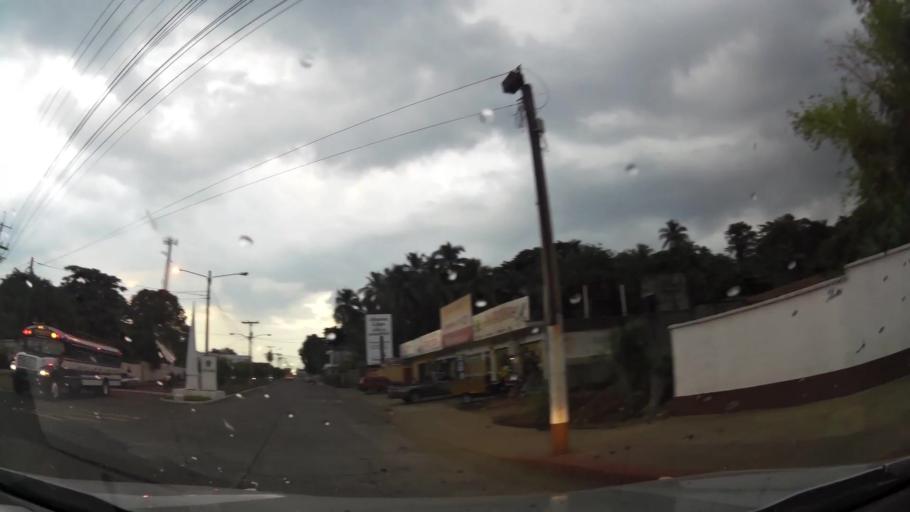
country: GT
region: Escuintla
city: Santa Lucia Cotzumalguapa
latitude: 14.3301
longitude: -91.0186
